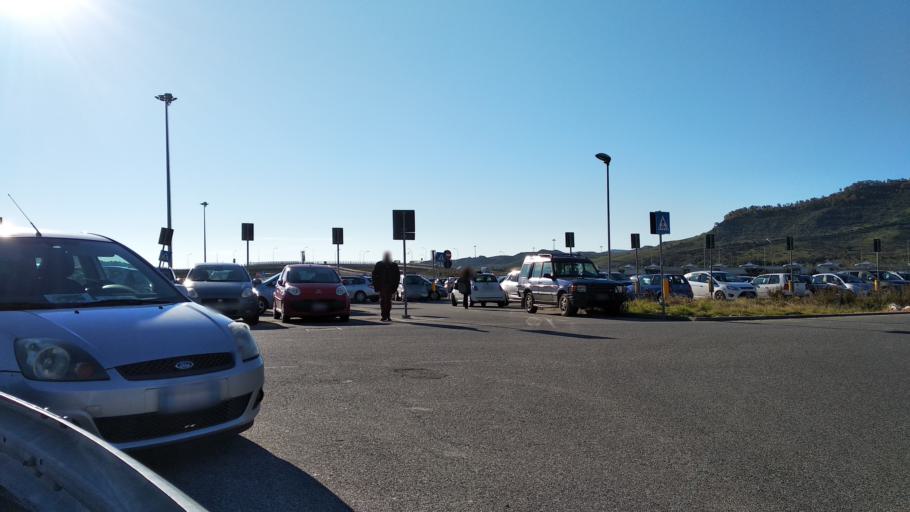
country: IT
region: Calabria
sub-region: Provincia di Catanzaro
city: Catanzaro
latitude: 38.8585
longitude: 16.5734
